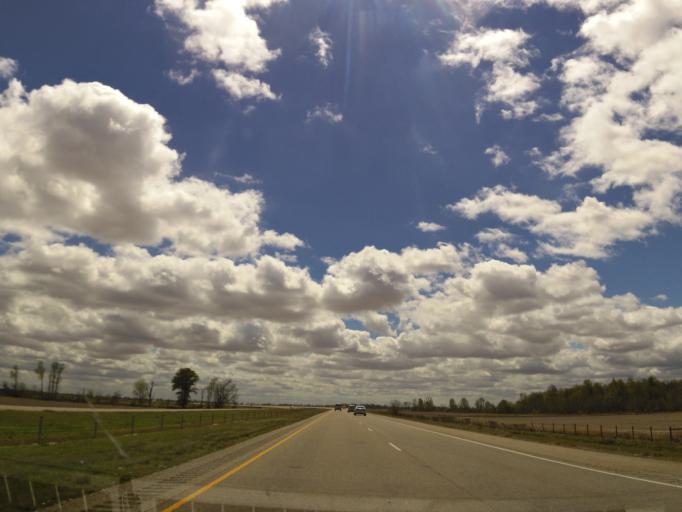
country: US
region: Arkansas
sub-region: Craighead County
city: Bay
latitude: 35.7220
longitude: -90.5800
